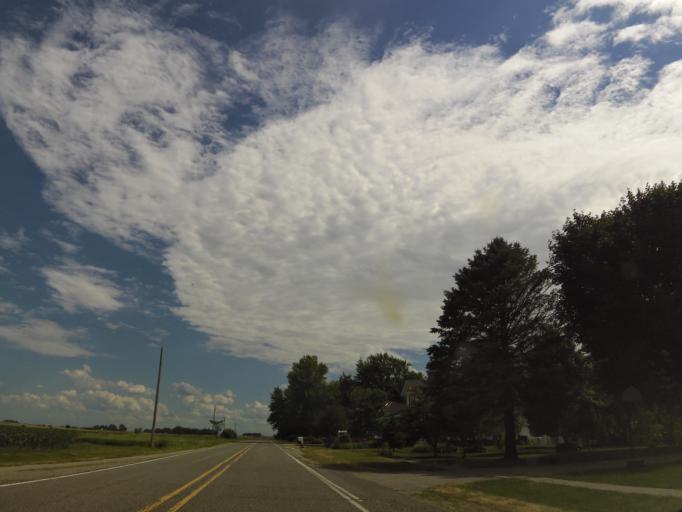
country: US
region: Iowa
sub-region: Henry County
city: Winfield
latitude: 41.1040
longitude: -91.5447
